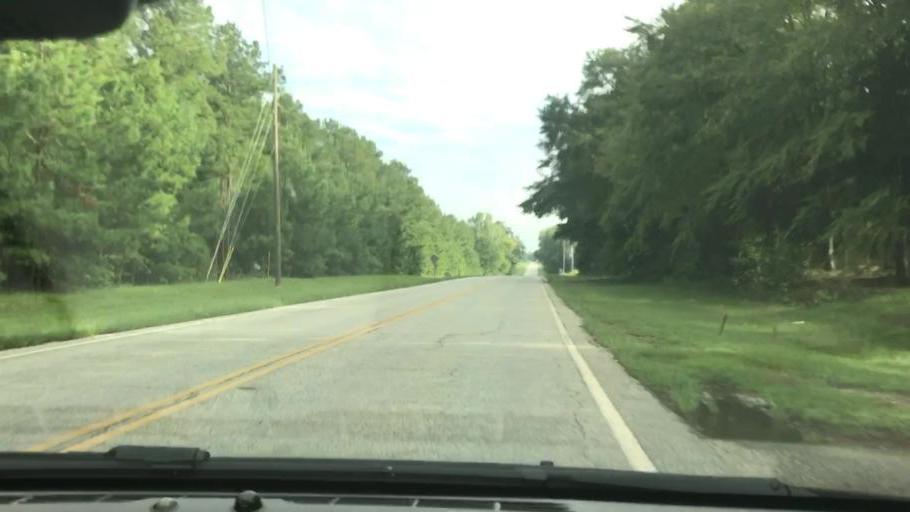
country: US
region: Georgia
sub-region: Quitman County
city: Georgetown
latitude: 31.7729
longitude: -85.0919
